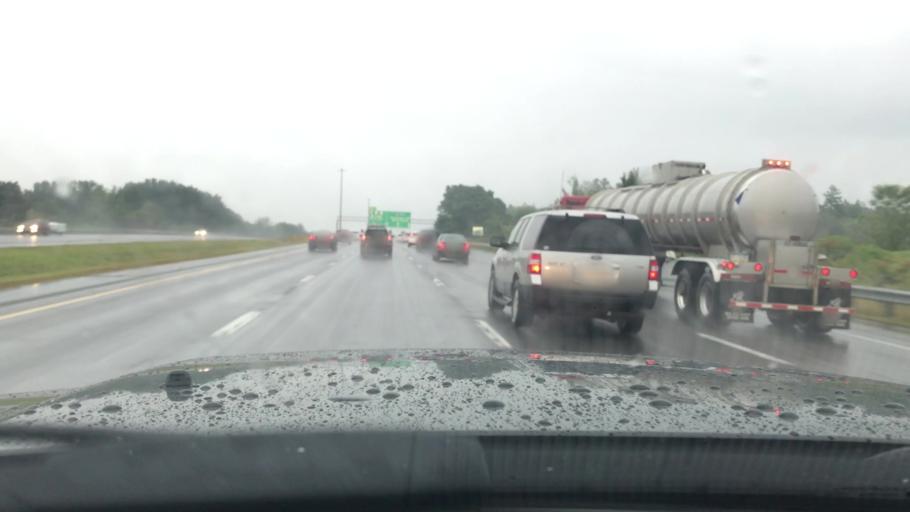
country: US
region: New Hampshire
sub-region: Rockingham County
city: Greenland
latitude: 43.0487
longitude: -70.8126
